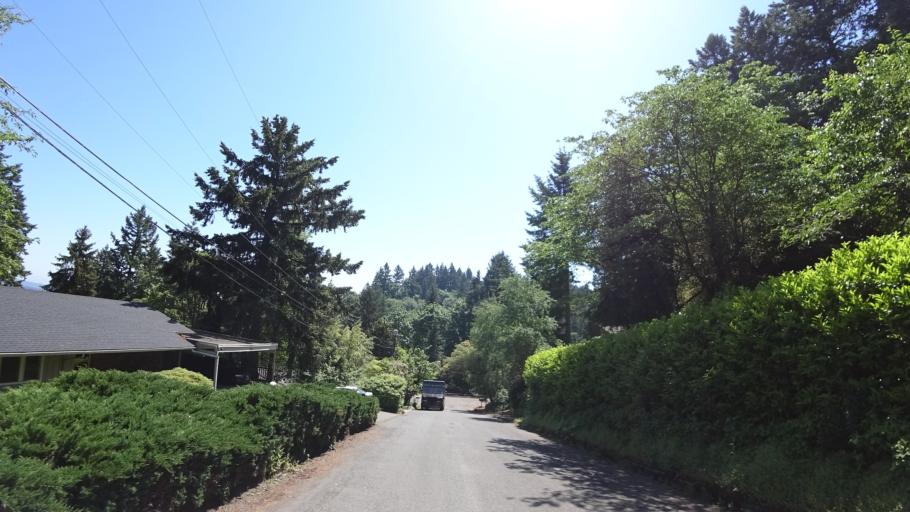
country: US
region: Oregon
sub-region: Multnomah County
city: Portland
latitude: 45.4811
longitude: -122.6819
